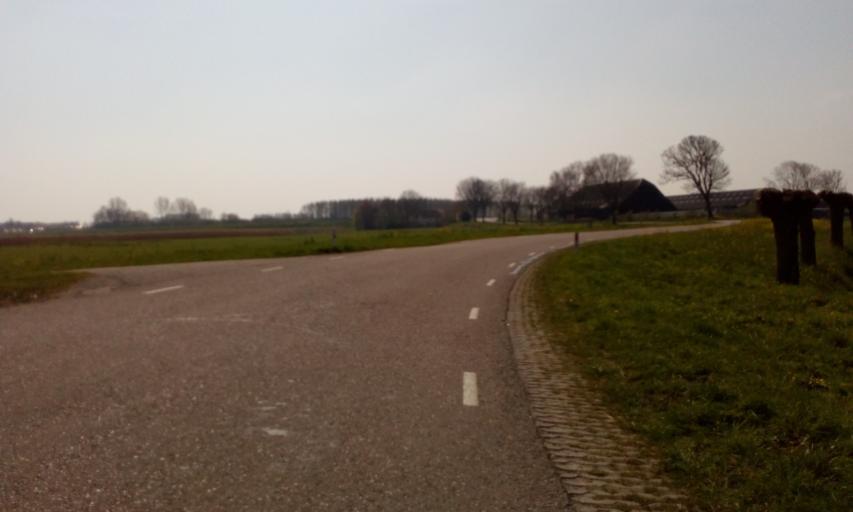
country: NL
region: South Holland
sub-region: Gemeente Spijkenisse
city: Spijkenisse
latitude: 51.8297
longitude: 4.2825
